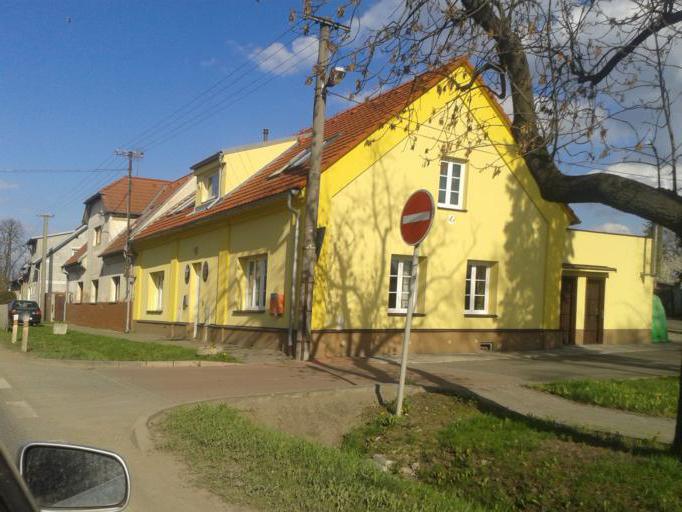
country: CZ
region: Central Bohemia
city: Rudna
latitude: 50.0451
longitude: 14.2597
